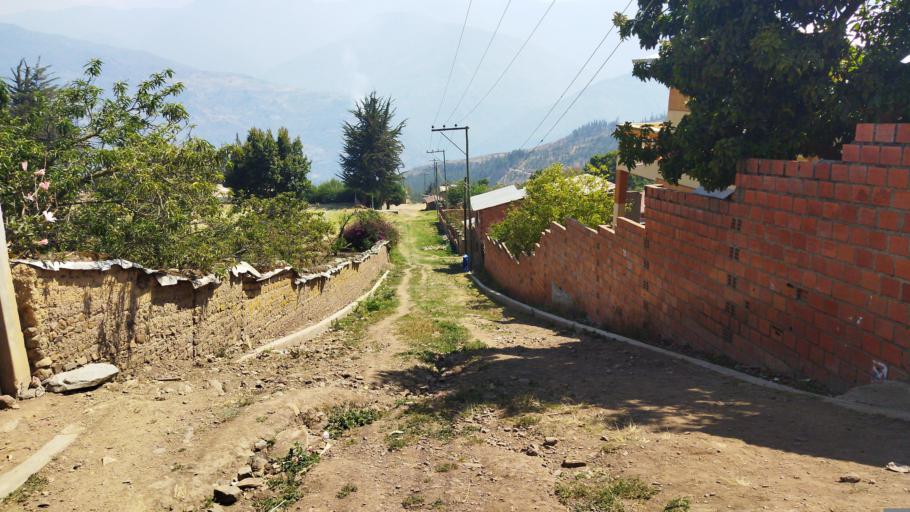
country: BO
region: La Paz
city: Quime
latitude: -16.9064
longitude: -67.1371
